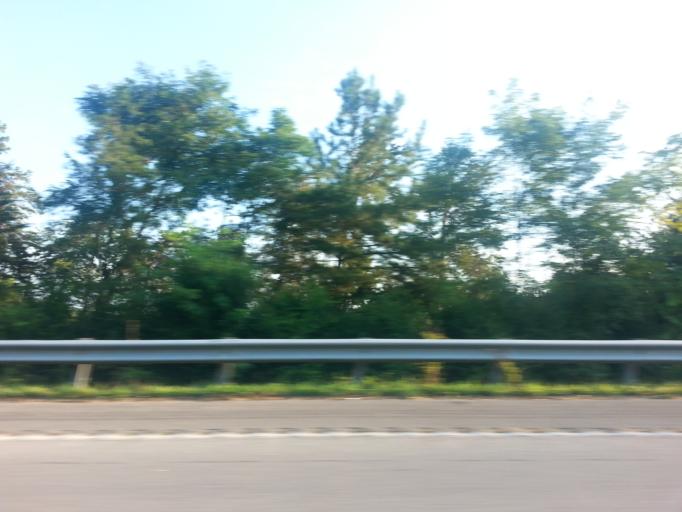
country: US
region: Tennessee
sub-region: McMinn County
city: Athens
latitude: 35.5152
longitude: -84.6266
